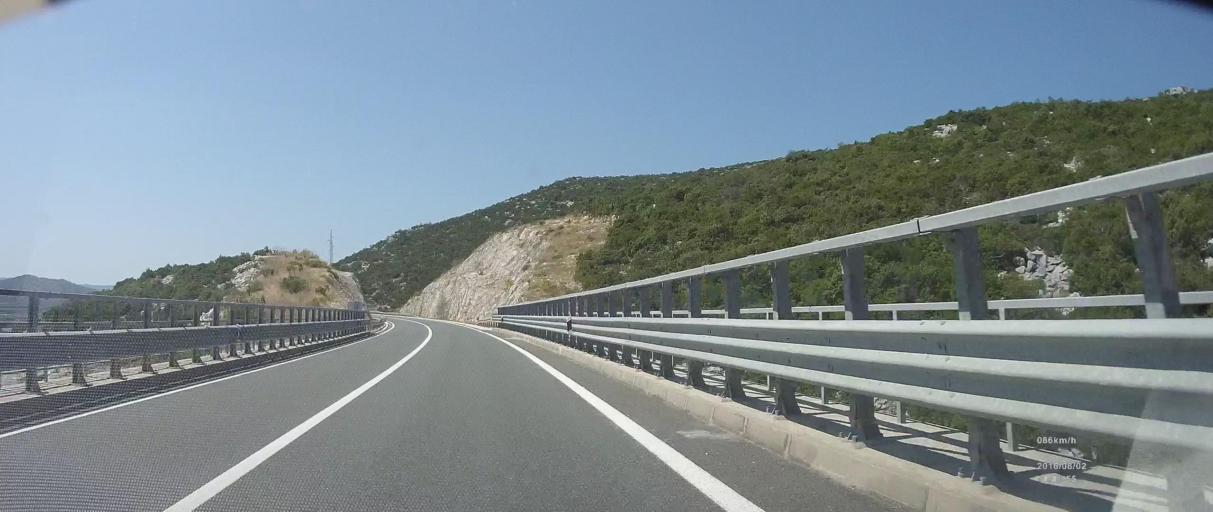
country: HR
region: Dubrovacko-Neretvanska
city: Komin
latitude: 43.0587
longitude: 17.4916
